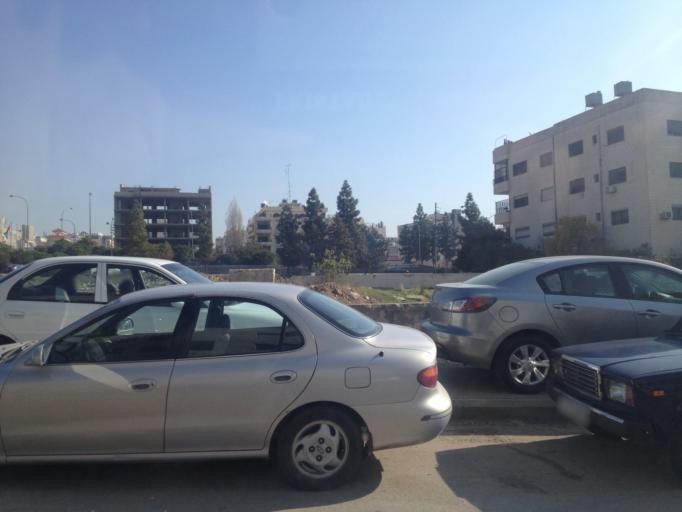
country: JO
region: Amman
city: Wadi as Sir
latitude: 31.9541
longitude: 35.8572
